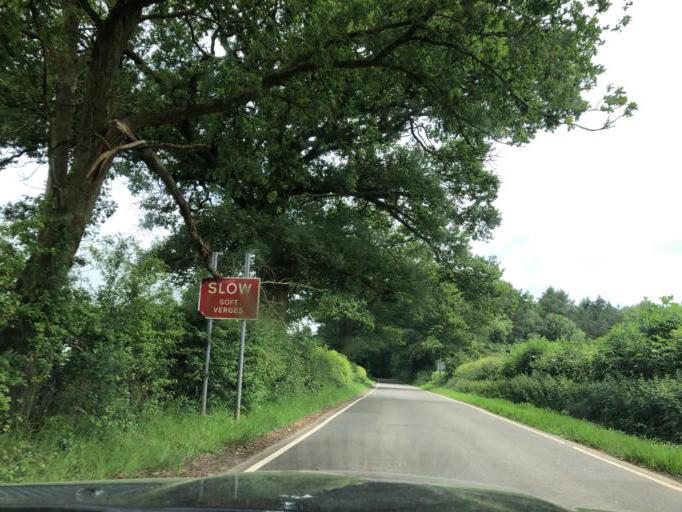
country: GB
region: England
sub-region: Warwickshire
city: Kenilworth
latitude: 52.3237
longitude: -1.5896
